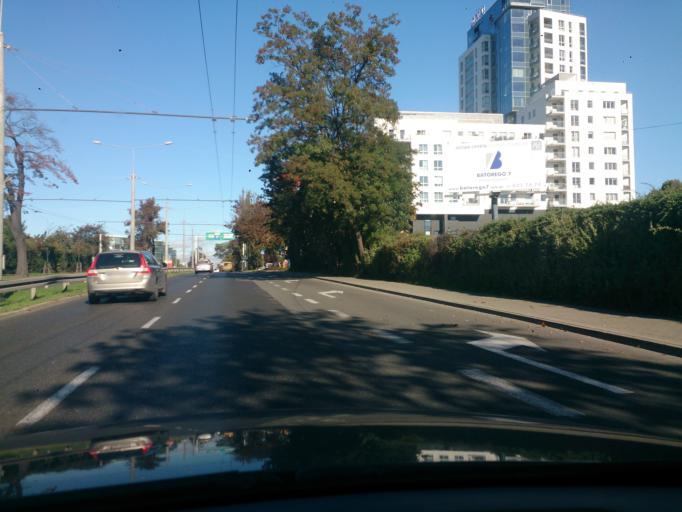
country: PL
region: Pomeranian Voivodeship
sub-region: Gdynia
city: Gdynia
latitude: 54.4897
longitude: 18.5426
